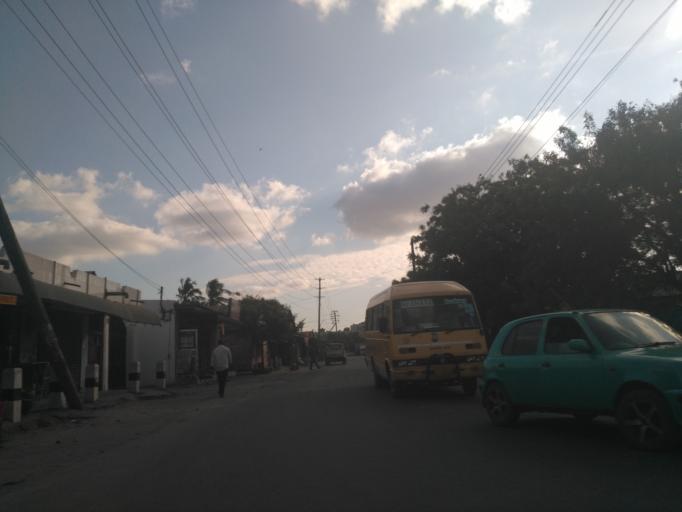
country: TZ
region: Dar es Salaam
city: Dar es Salaam
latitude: -6.8620
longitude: 39.2582
